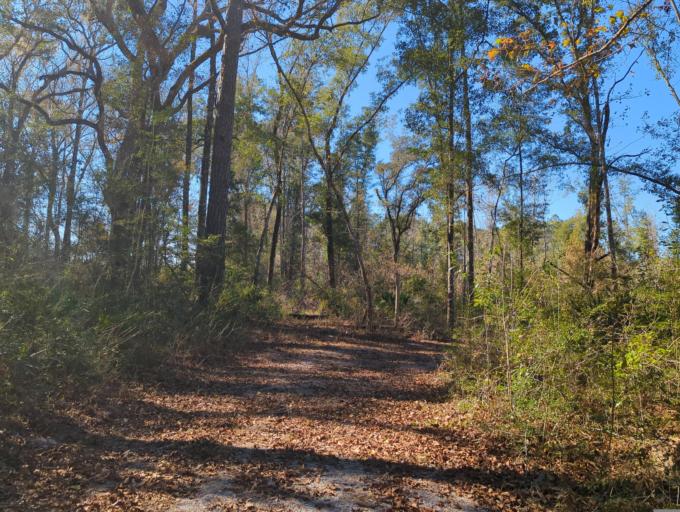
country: US
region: Florida
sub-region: Wakulla County
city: Crawfordville
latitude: 30.1823
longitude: -84.3320
